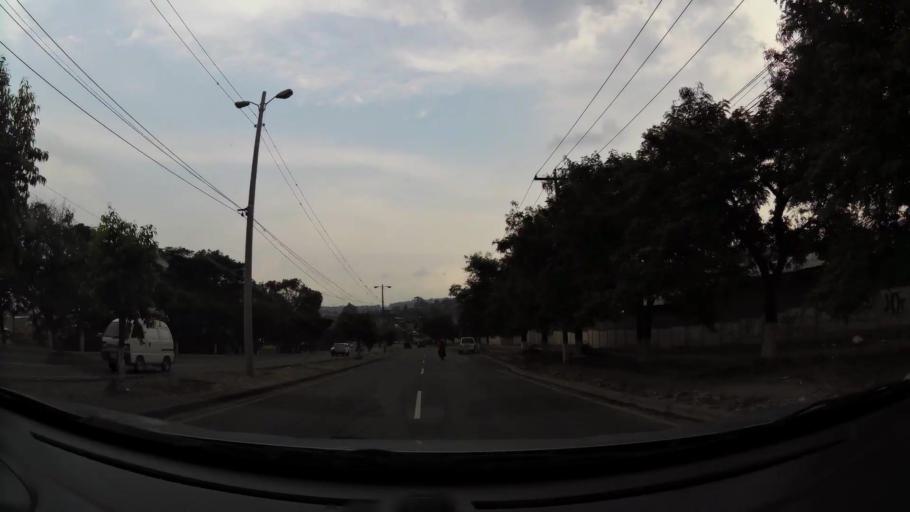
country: HN
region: Francisco Morazan
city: El Lolo
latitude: 14.0991
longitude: -87.2408
